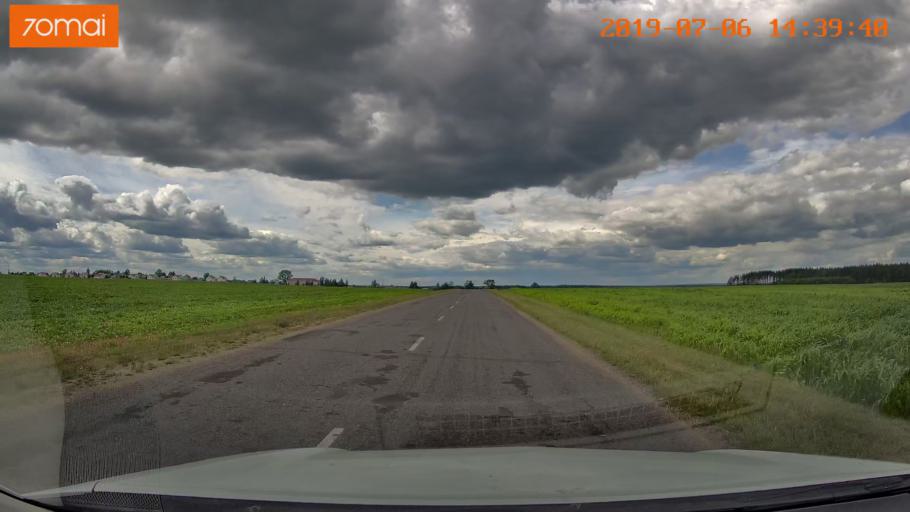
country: BY
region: Minsk
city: Ivyanyets
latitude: 53.9186
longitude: 26.6849
